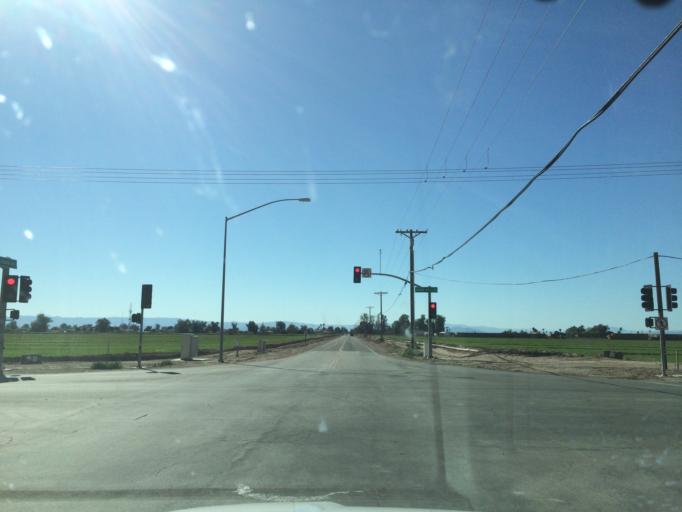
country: US
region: California
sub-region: Imperial County
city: Heber
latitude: 32.7524
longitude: -115.5516
